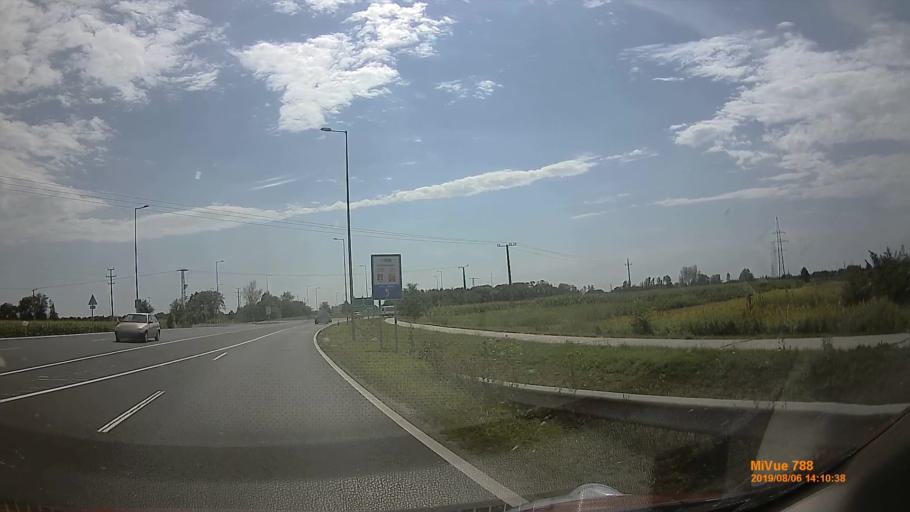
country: HU
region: Vas
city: Szombathely
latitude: 47.2221
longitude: 16.6583
